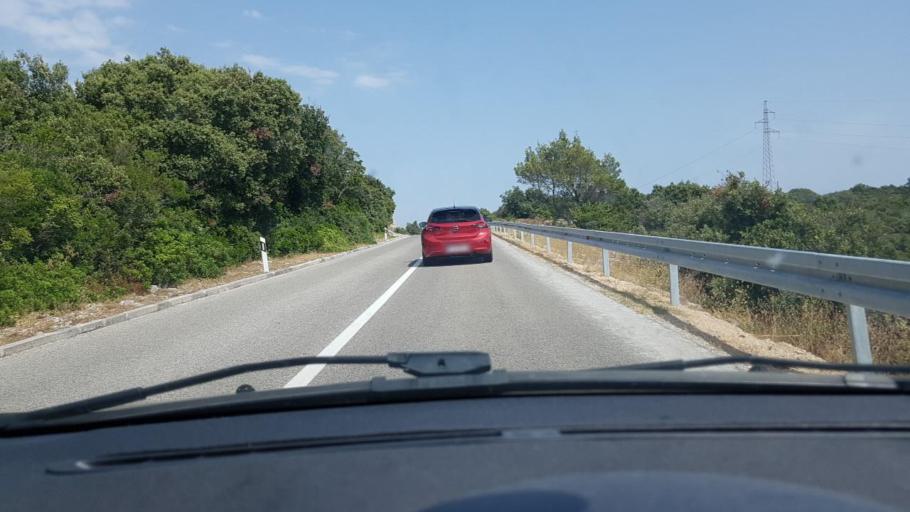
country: HR
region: Dubrovacko-Neretvanska
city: Smokvica
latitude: 42.9487
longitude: 16.9775
